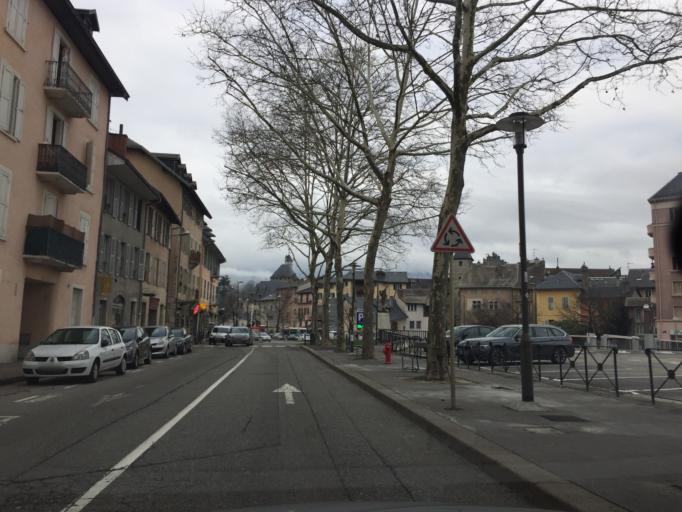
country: FR
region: Rhone-Alpes
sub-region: Departement de la Savoie
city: Chambery
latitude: 45.5630
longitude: 5.9234
